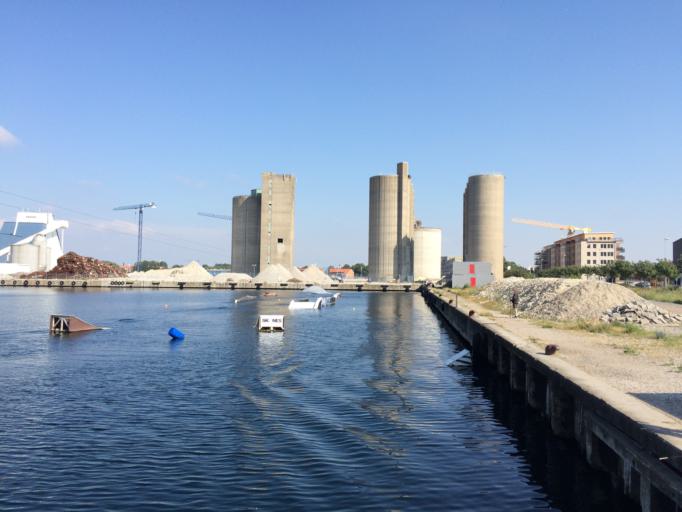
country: SE
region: Skane
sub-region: Malmo
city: Bunkeflostrand
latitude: 55.5892
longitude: 12.9235
